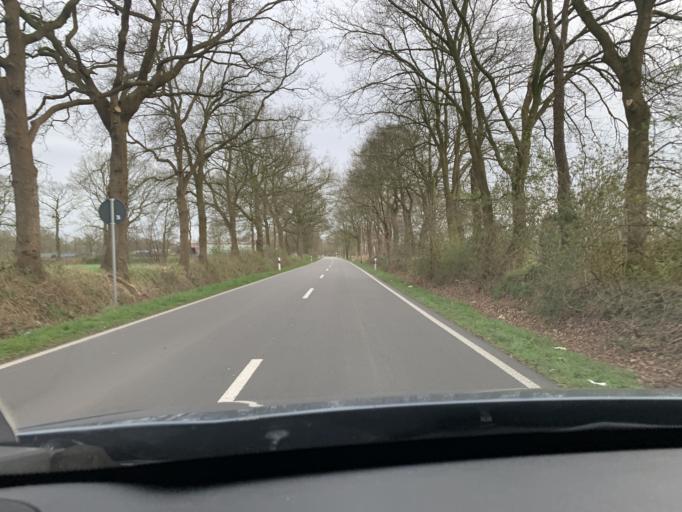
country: DE
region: Lower Saxony
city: Schwerinsdorf
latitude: 53.2657
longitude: 7.7082
